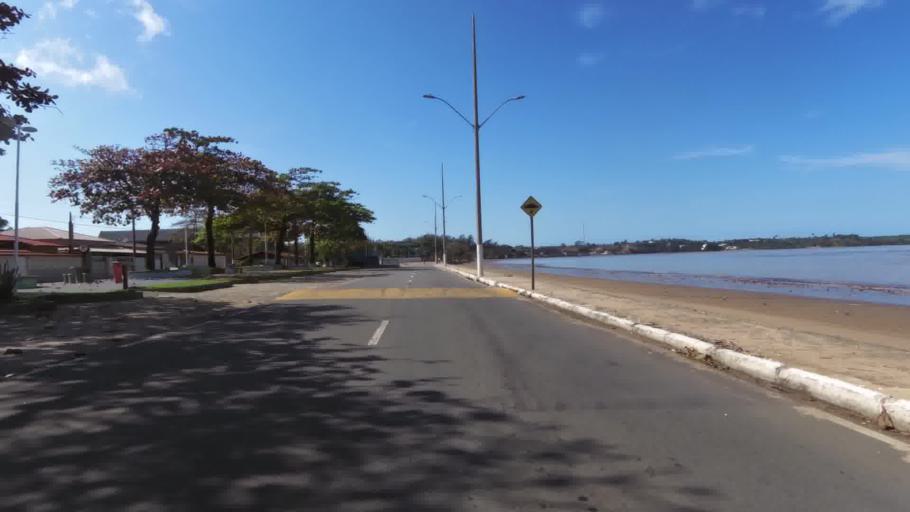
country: BR
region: Espirito Santo
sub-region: Piuma
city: Piuma
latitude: -20.8119
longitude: -40.6370
